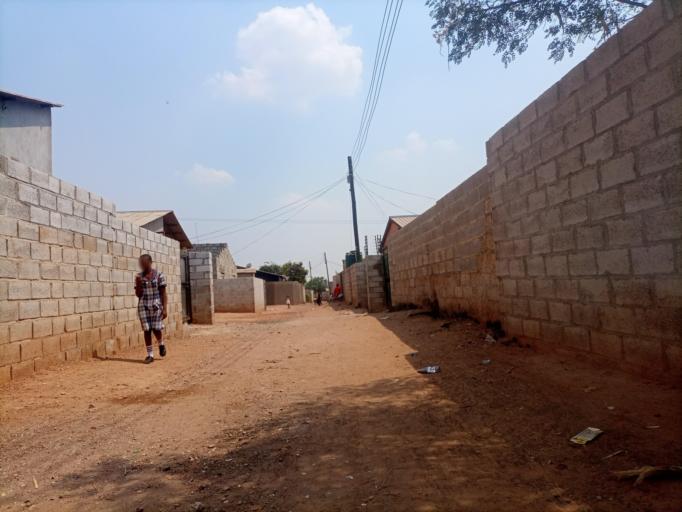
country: ZM
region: Lusaka
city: Lusaka
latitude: -15.4039
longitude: 28.3762
